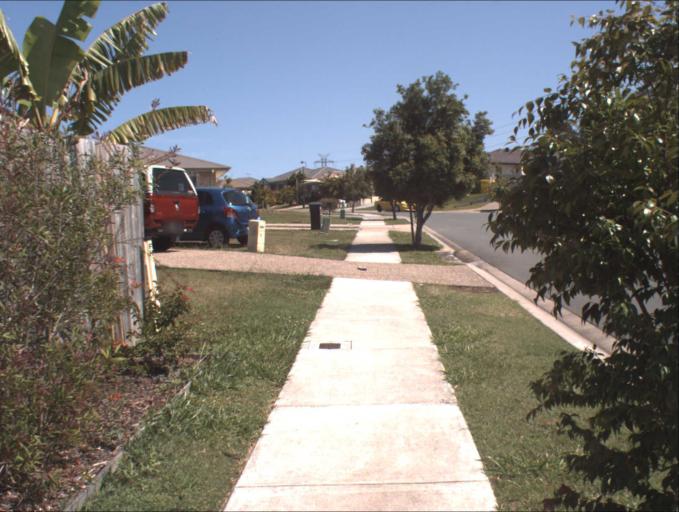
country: AU
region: Queensland
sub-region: Logan
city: Woodridge
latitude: -27.6620
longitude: 153.0863
